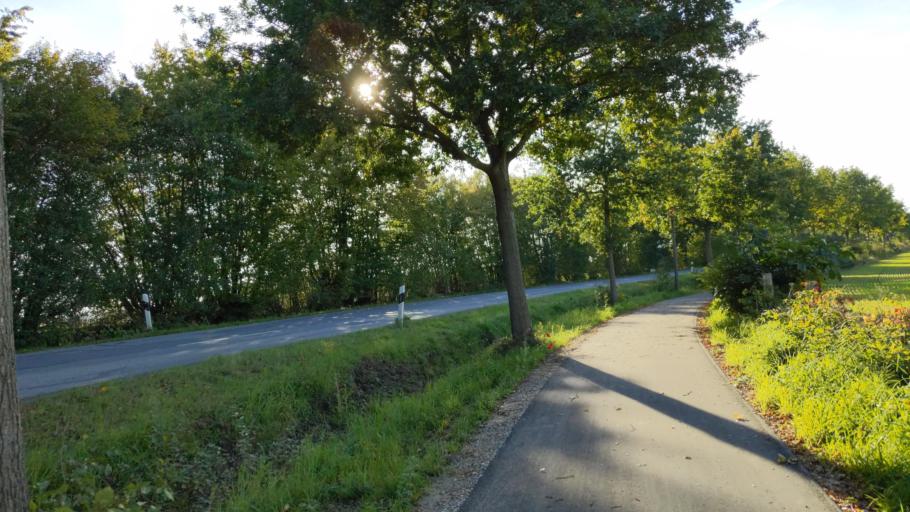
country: DE
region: Schleswig-Holstein
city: Susel
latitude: 54.1089
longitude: 10.6784
